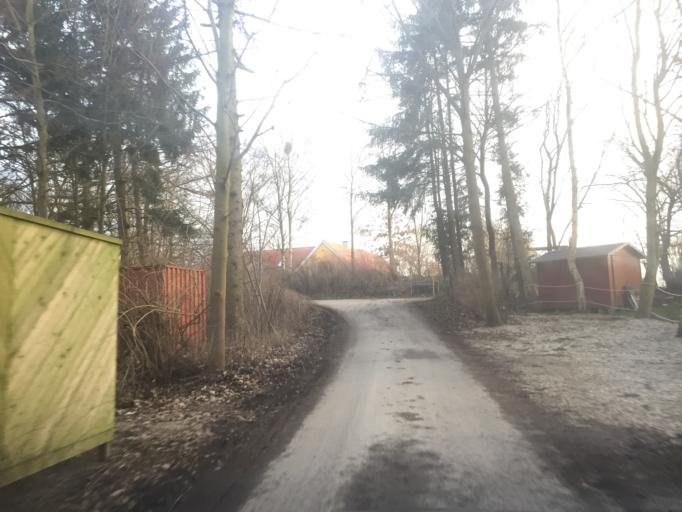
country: DK
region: Capital Region
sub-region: Egedal Kommune
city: Smorumnedre
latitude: 55.7037
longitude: 12.2686
